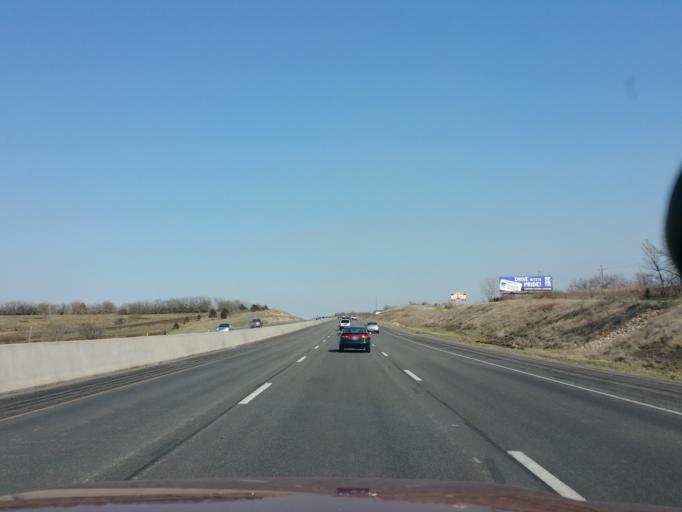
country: US
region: Kansas
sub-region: Douglas County
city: Lawrence
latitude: 39.0009
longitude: -95.4206
